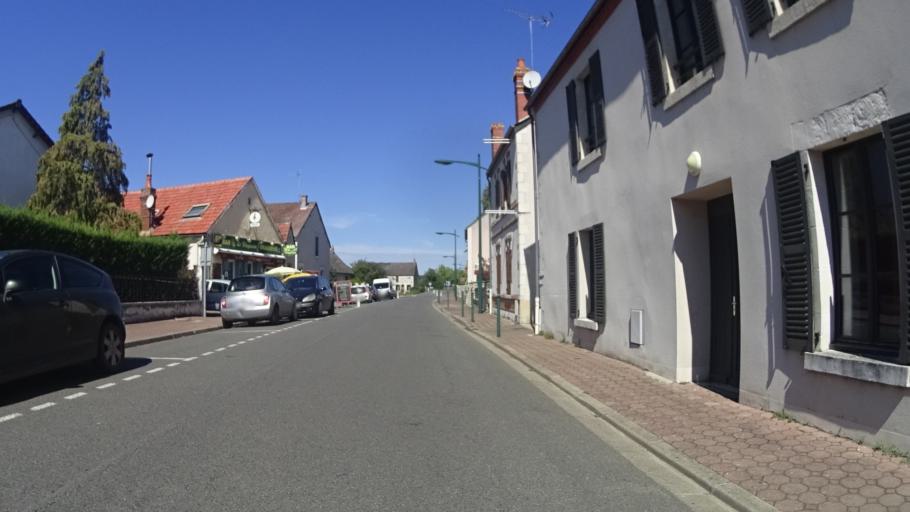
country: FR
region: Centre
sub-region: Departement du Cher
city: Belleville-sur-Loire
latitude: 47.5082
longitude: 2.8508
